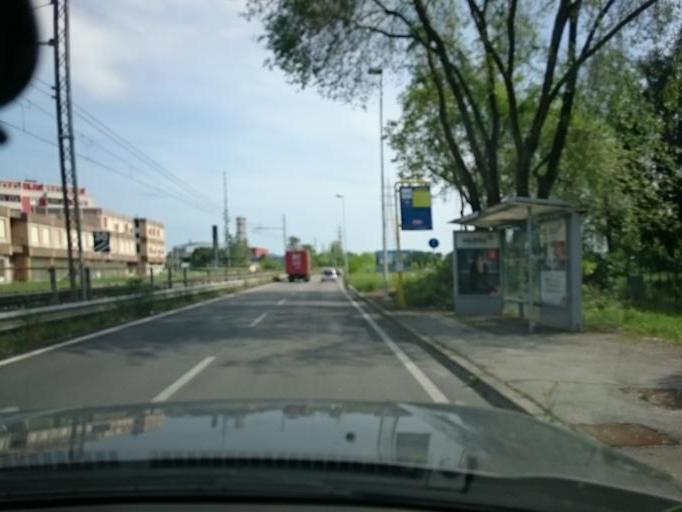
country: IT
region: Veneto
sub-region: Provincia di Padova
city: Padova
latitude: 45.4123
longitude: 11.9165
